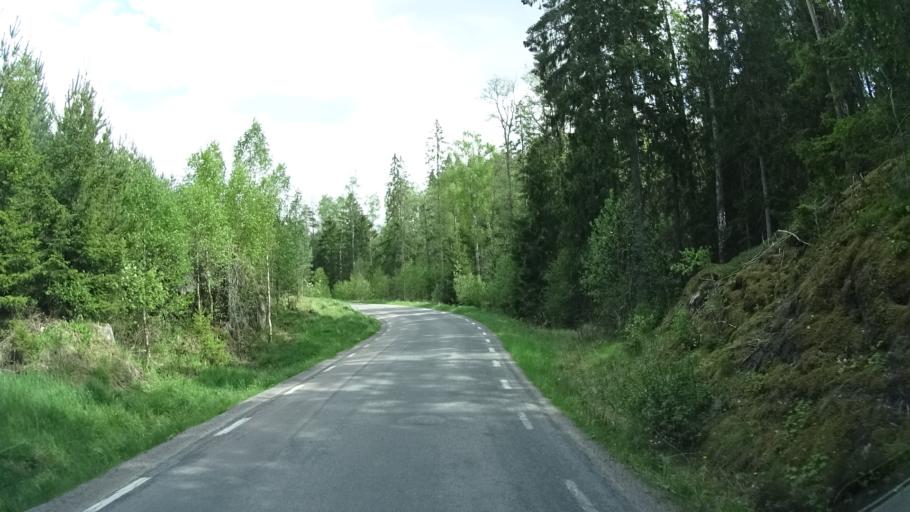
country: SE
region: OEstergoetland
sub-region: Finspangs Kommun
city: Finspang
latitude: 58.6097
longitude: 15.7315
